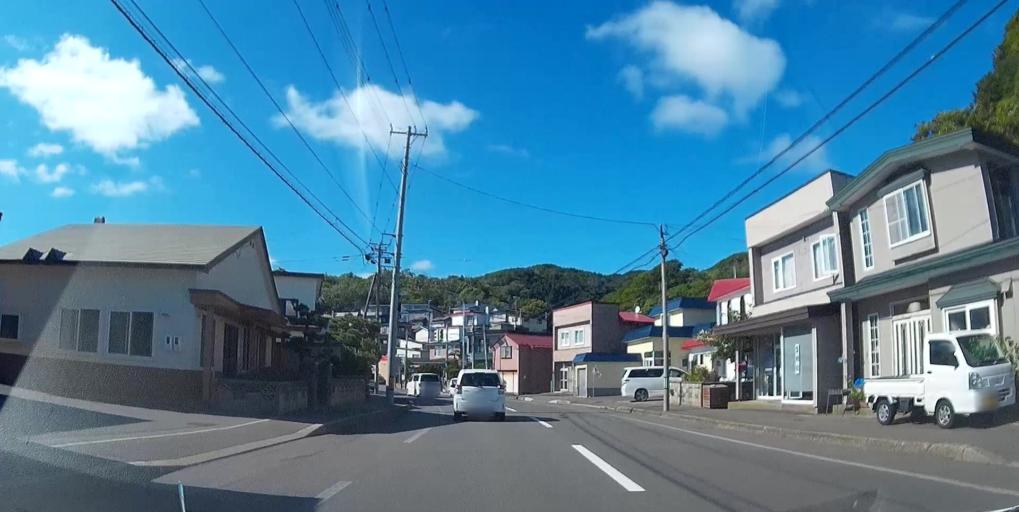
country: JP
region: Hokkaido
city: Kamiiso
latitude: 42.0461
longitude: 140.0846
